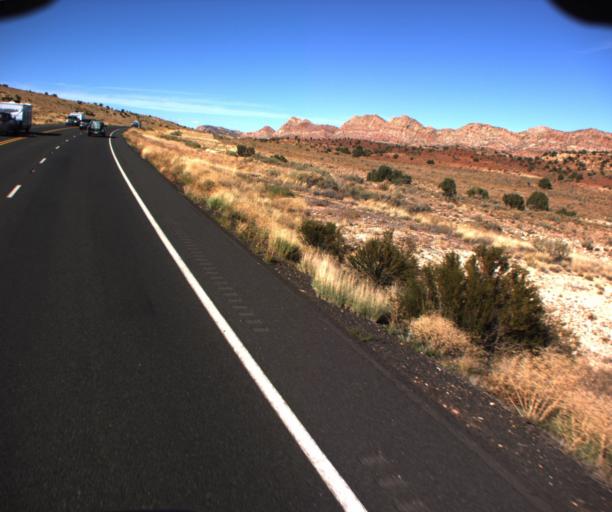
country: US
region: Arizona
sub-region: Coconino County
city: Tuba City
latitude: 36.3474
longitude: -111.5040
